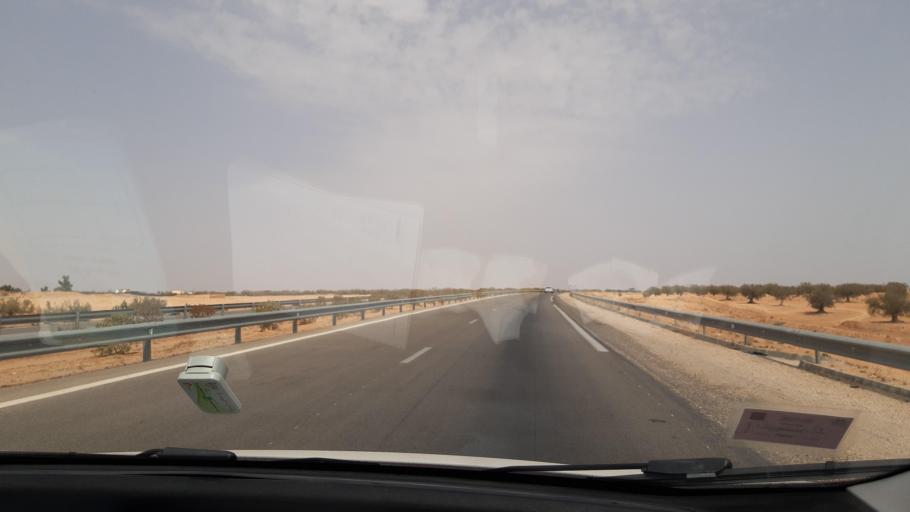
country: TN
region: Safaqis
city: Bi'r `Ali Bin Khalifah
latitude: 34.5628
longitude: 10.3432
